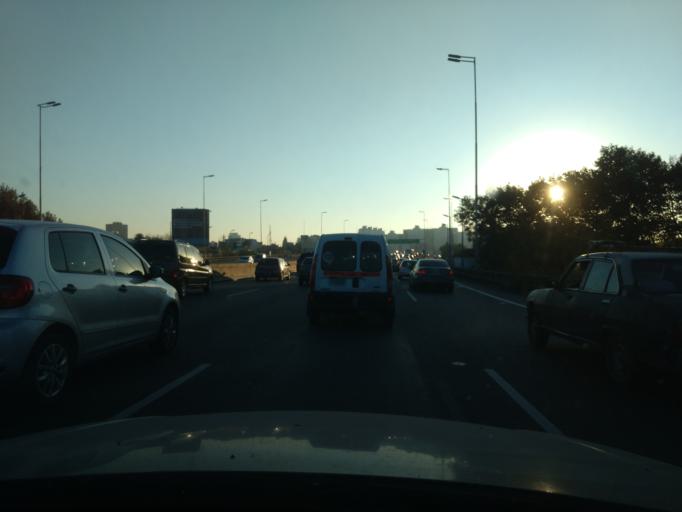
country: AR
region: Buenos Aires F.D.
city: Villa Santa Rita
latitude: -34.6387
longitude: -58.4563
